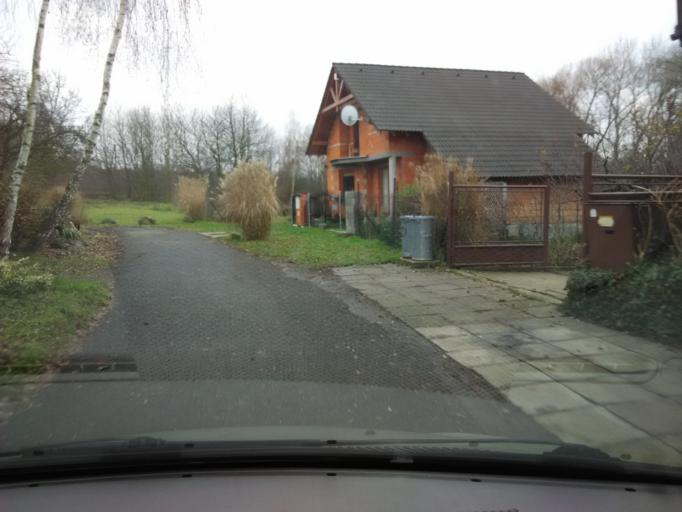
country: SK
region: Nitriansky
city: Tlmace
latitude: 48.3127
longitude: 18.5178
